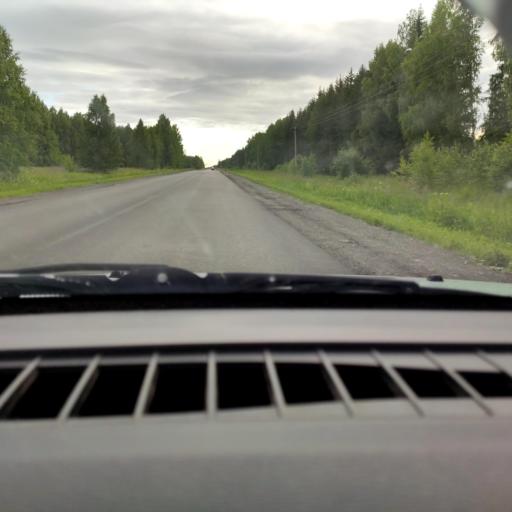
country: RU
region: Perm
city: Orda
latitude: 57.2281
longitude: 56.9636
